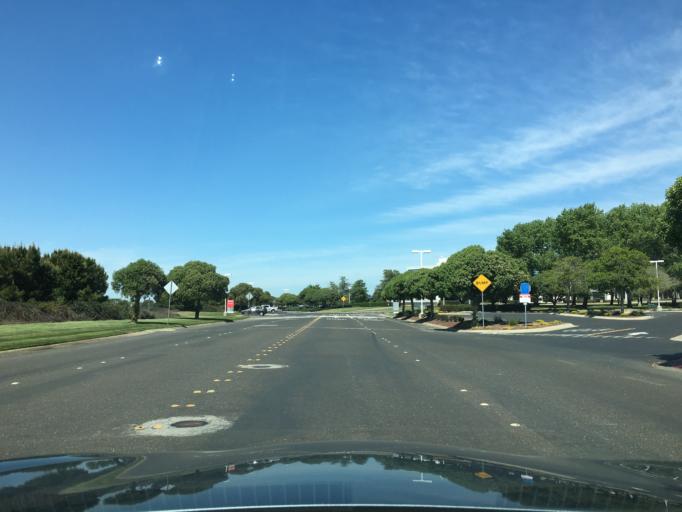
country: US
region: California
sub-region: San Mateo County
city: Redwood Shores
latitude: 37.5349
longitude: -122.2591
